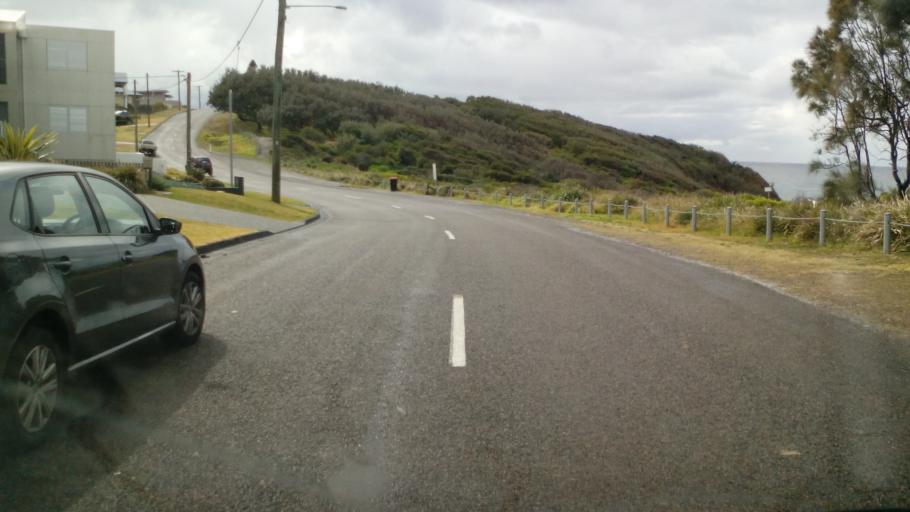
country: AU
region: New South Wales
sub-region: Lake Macquarie Shire
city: Belmont South
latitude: -33.0961
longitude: 151.6573
